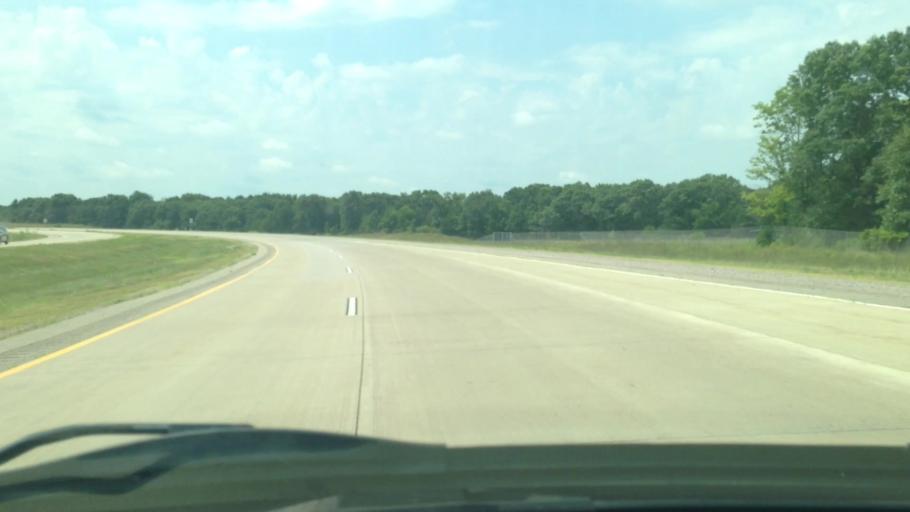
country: US
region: Wisconsin
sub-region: Sauk County
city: Lake Delton
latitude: 43.5549
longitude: -89.7857
